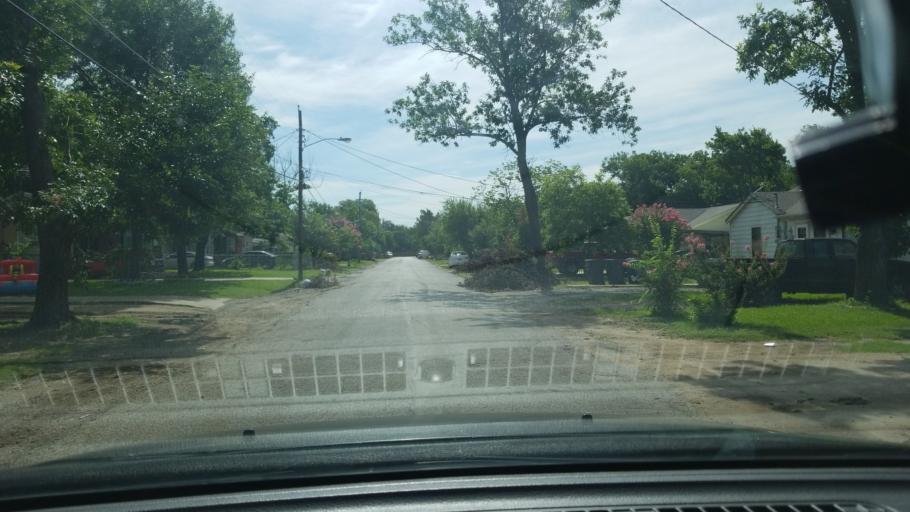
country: US
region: Texas
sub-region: Dallas County
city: Balch Springs
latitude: 32.7675
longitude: -96.6810
